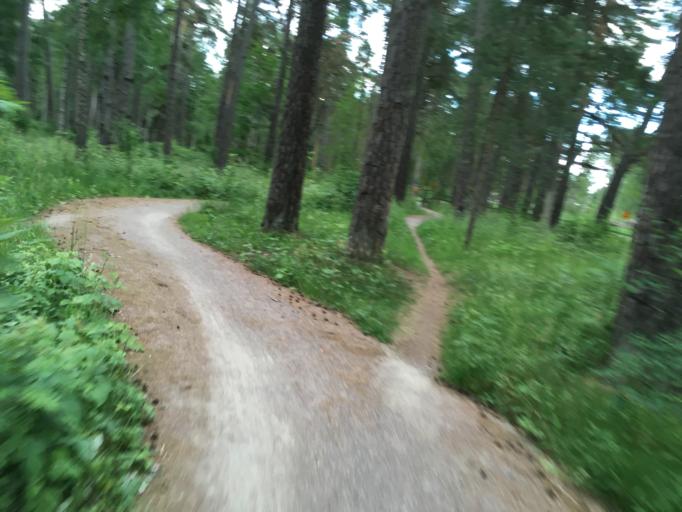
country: SE
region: Uppsala
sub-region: Uppsala Kommun
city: Uppsala
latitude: 59.8365
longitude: 17.6388
